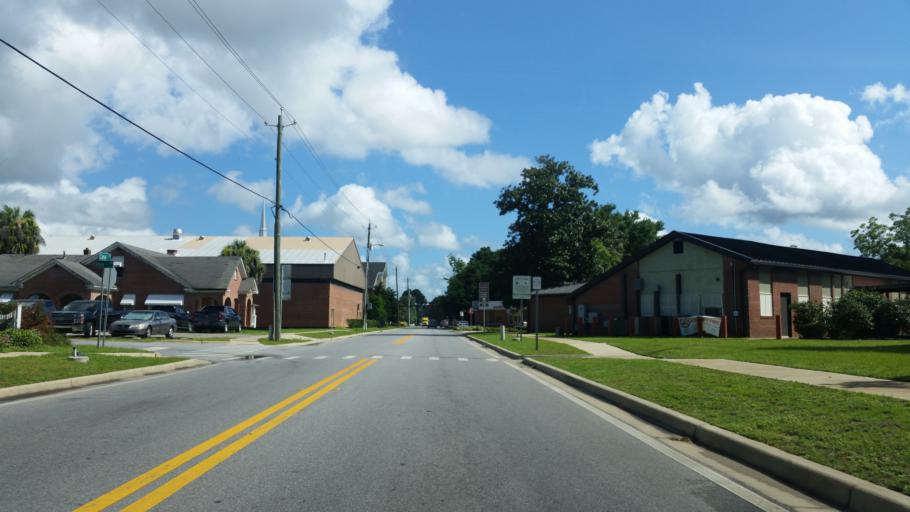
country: US
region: Florida
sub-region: Santa Rosa County
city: Milton
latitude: 30.6194
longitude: -87.0390
